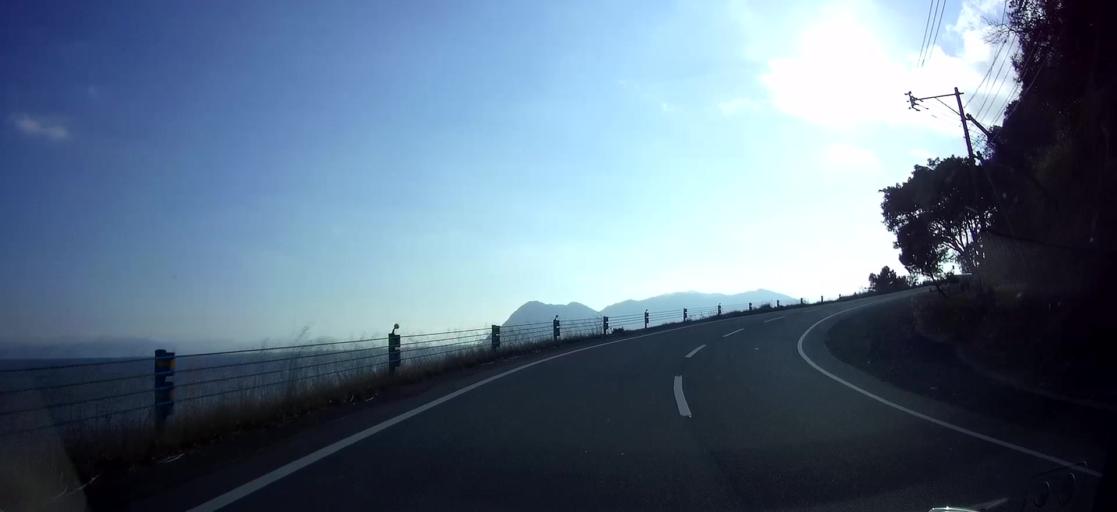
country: JP
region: Kumamoto
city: Minamata
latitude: 32.3836
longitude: 130.3819
